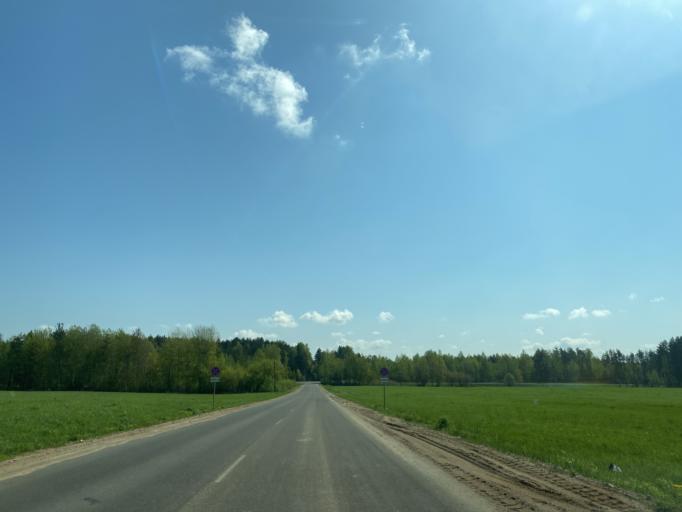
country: BY
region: Minsk
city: Horad Barysaw
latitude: 54.1793
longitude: 28.5667
